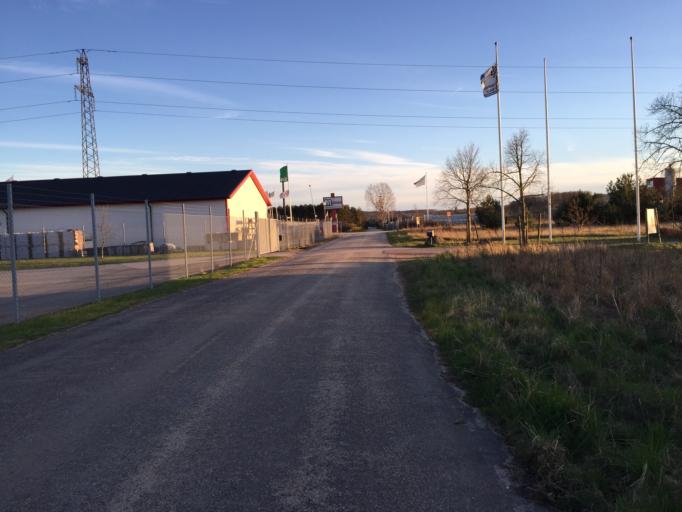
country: SE
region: Skane
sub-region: Lunds Kommun
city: Veberod
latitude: 55.6433
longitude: 13.4971
